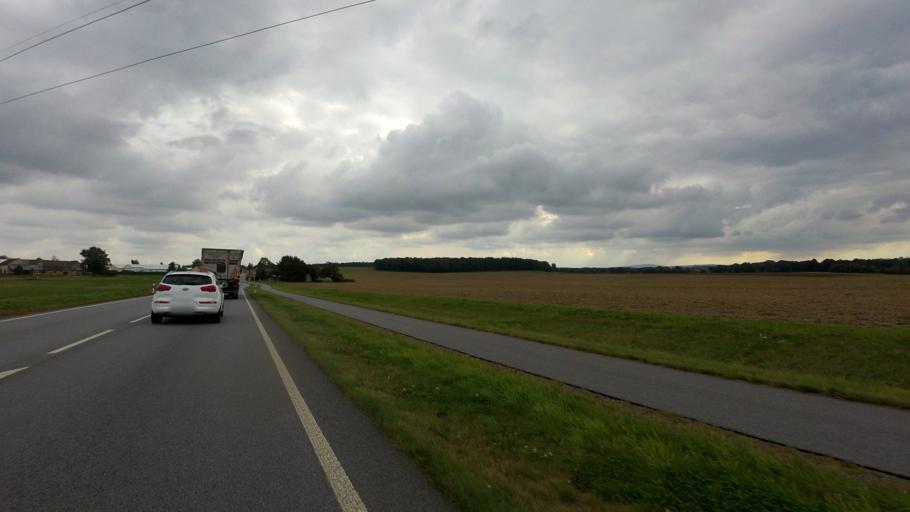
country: DE
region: Saxony
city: Radibor
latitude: 51.2398
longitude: 14.3671
